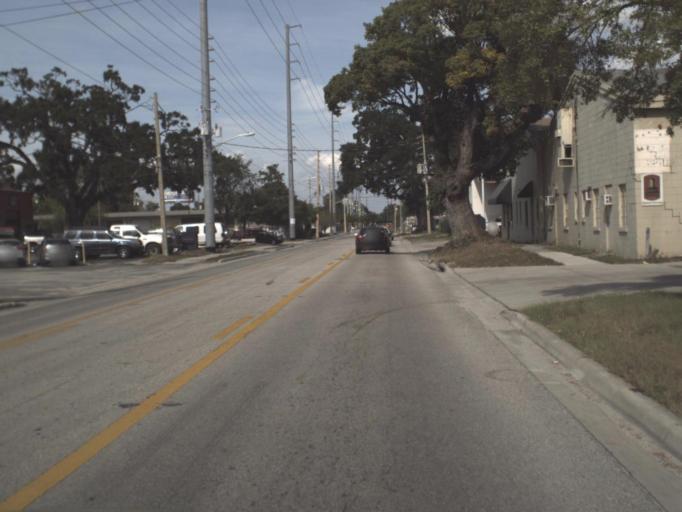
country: US
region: Florida
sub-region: Orange County
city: Orlando
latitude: 28.5210
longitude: -81.3846
